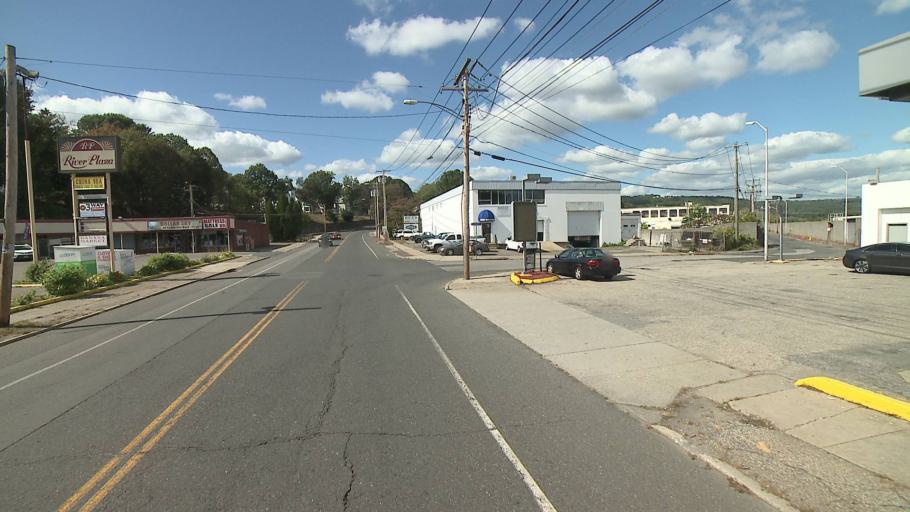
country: US
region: Connecticut
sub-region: New Haven County
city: Ansonia
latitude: 41.3457
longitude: -73.0826
